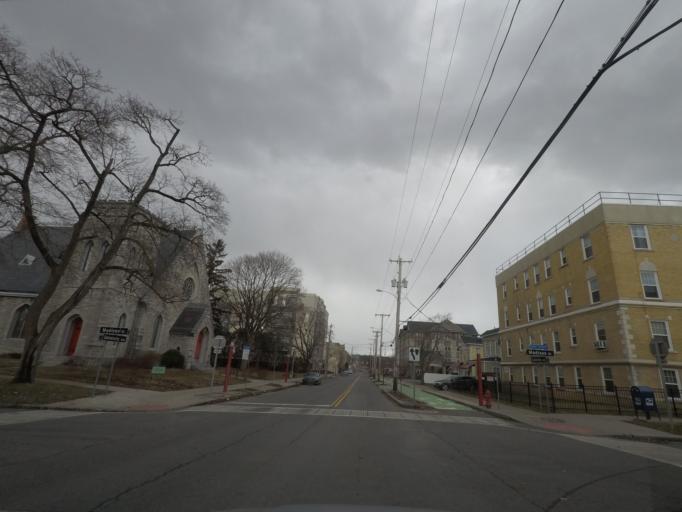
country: US
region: New York
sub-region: Onondaga County
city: Syracuse
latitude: 43.0453
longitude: -76.1343
